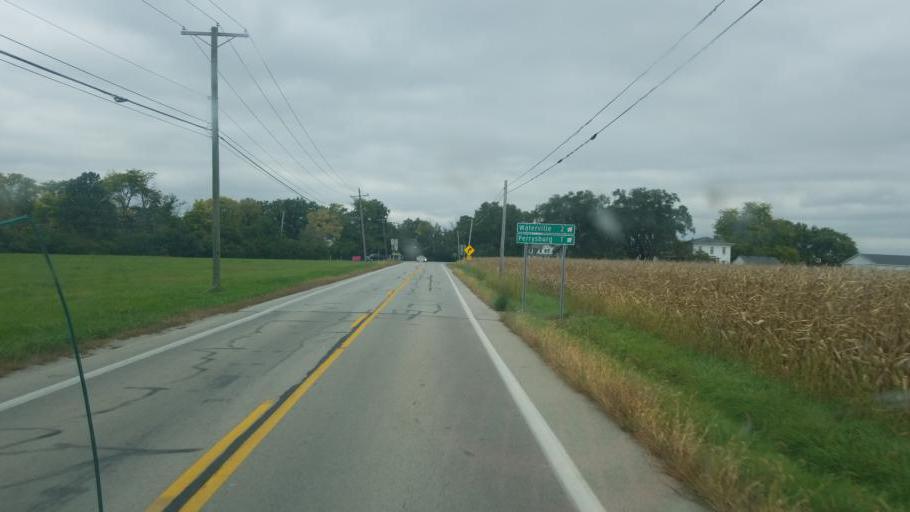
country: US
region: Ohio
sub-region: Lucas County
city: Waterville
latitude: 41.4904
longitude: -83.7112
